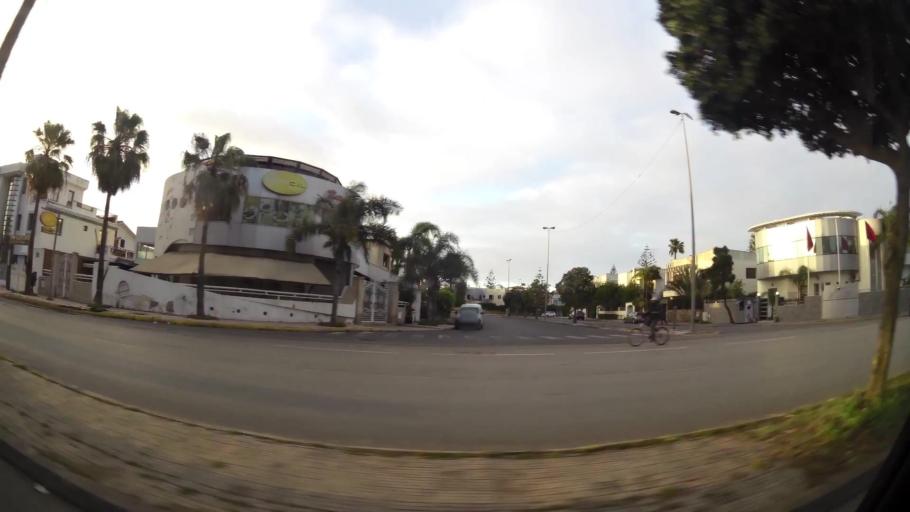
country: MA
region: Grand Casablanca
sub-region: Casablanca
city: Casablanca
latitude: 33.5702
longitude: -7.6663
